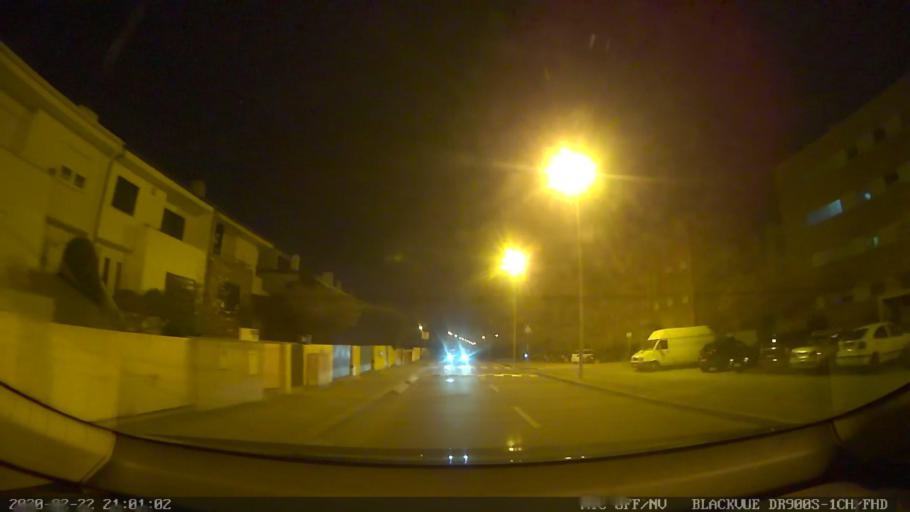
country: PT
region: Porto
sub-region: Matosinhos
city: Senhora da Hora
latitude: 41.1890
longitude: -8.6397
